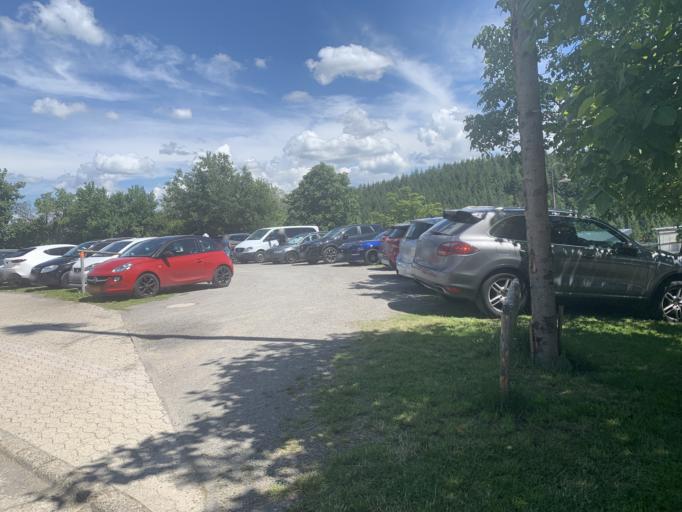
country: DE
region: Rheinland-Pfalz
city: Sosberg
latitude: 50.0757
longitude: 7.3396
